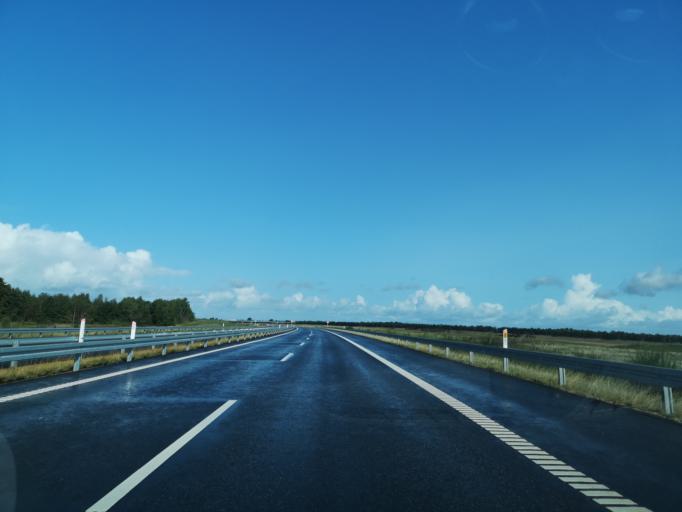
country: DK
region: Central Jutland
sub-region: Herning Kommune
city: Snejbjerg
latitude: 56.1895
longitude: 8.8894
